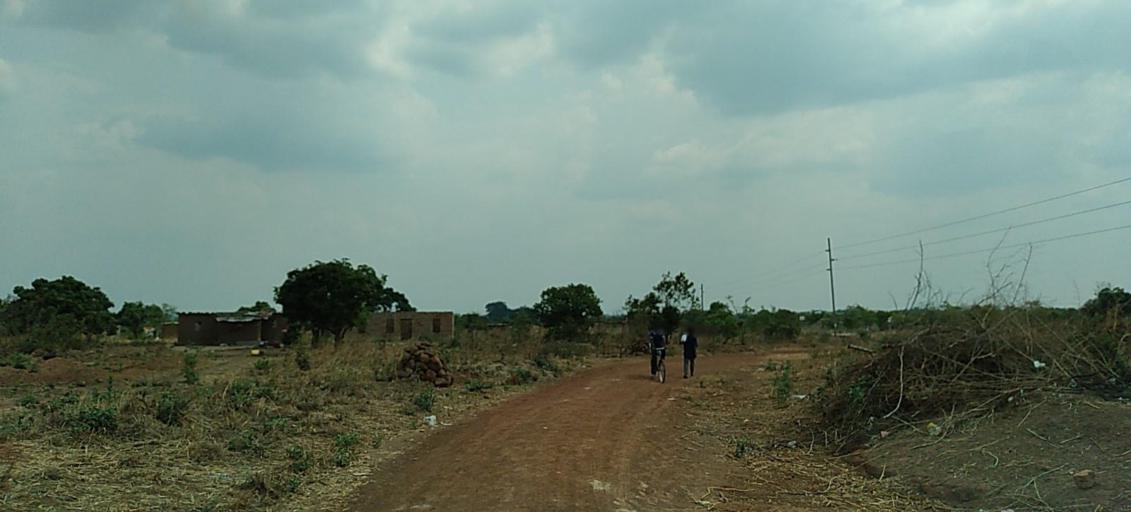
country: ZM
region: Copperbelt
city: Kalulushi
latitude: -12.8732
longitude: 28.0777
